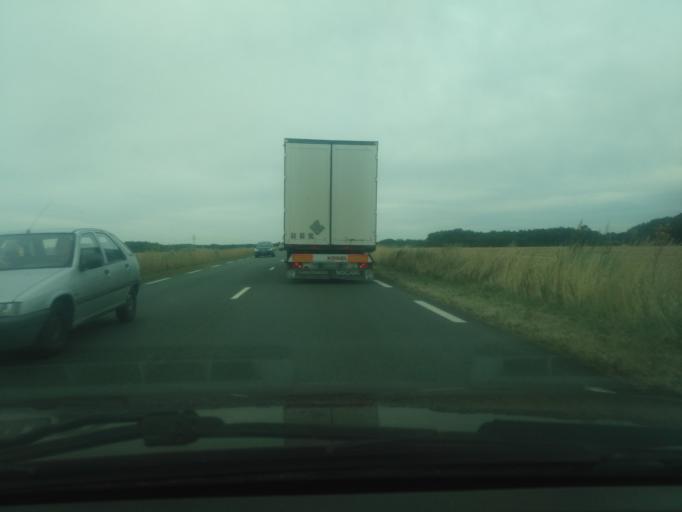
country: FR
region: Poitou-Charentes
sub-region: Departement de la Vienne
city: Bonnes
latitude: 46.5655
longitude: 0.5960
